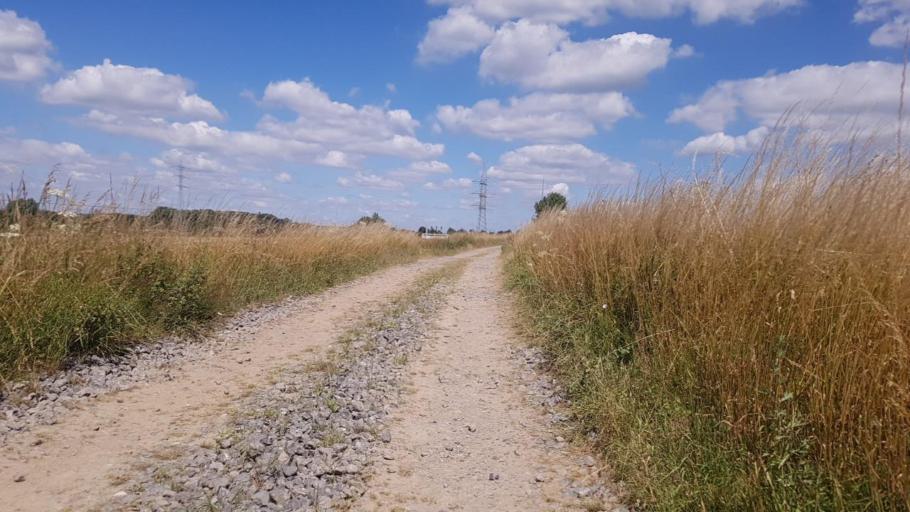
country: BE
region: Wallonia
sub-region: Province du Hainaut
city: Thuin
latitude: 50.3100
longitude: 4.3428
